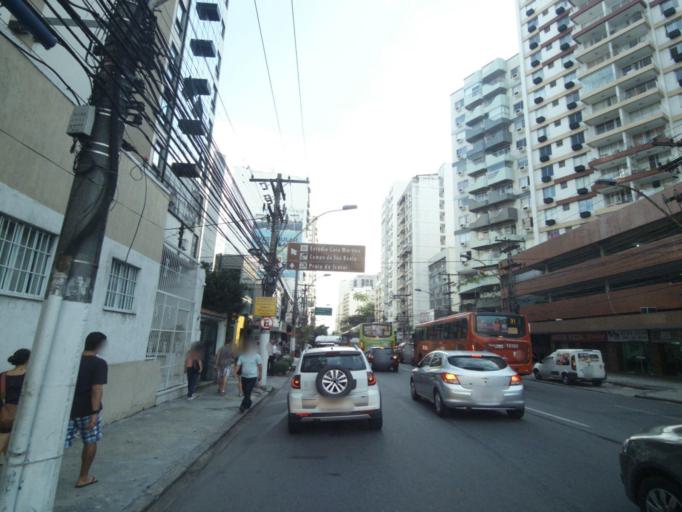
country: BR
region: Rio de Janeiro
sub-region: Niteroi
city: Niteroi
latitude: -22.9005
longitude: -43.1126
